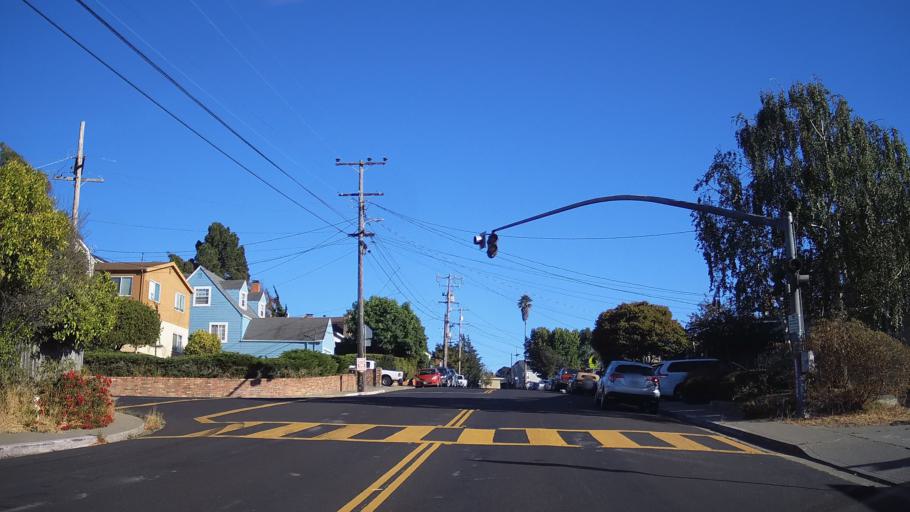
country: US
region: California
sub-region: Contra Costa County
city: East Richmond Heights
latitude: 37.9422
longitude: -122.3134
